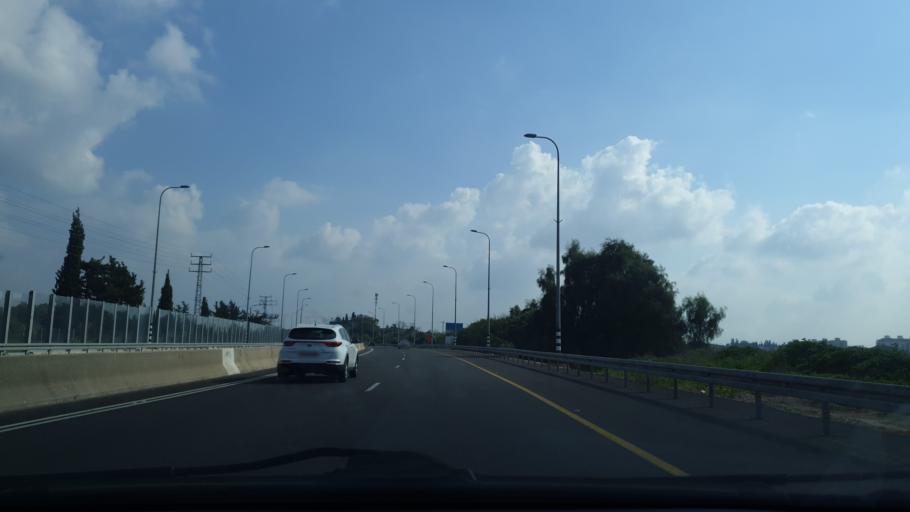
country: IL
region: Central District
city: Ramla
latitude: 31.9482
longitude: 34.8583
